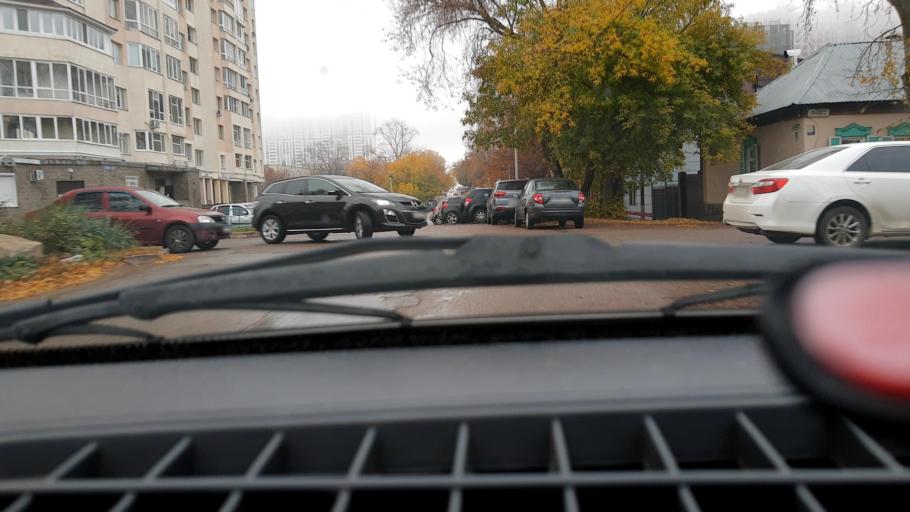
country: RU
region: Bashkortostan
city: Ufa
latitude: 54.7326
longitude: 55.9246
